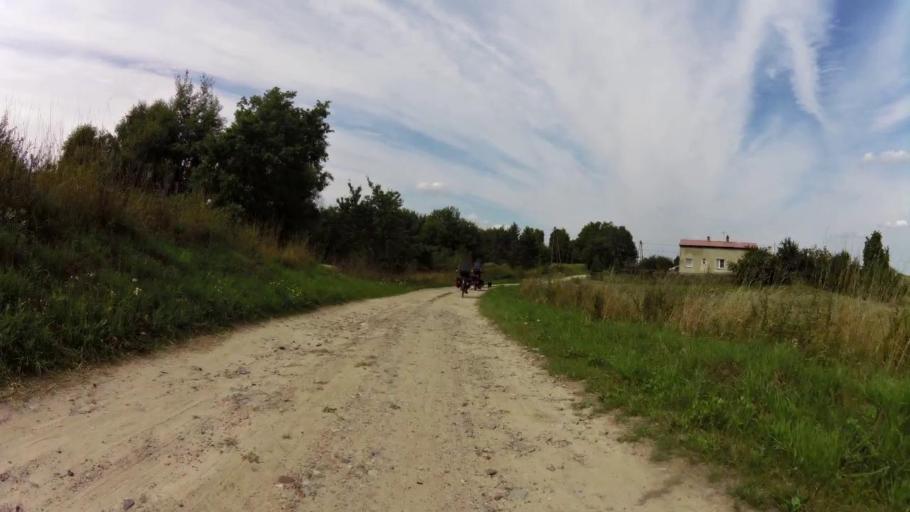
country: PL
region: West Pomeranian Voivodeship
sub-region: Powiat lobeski
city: Wegorzyno
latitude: 53.5293
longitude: 15.6151
